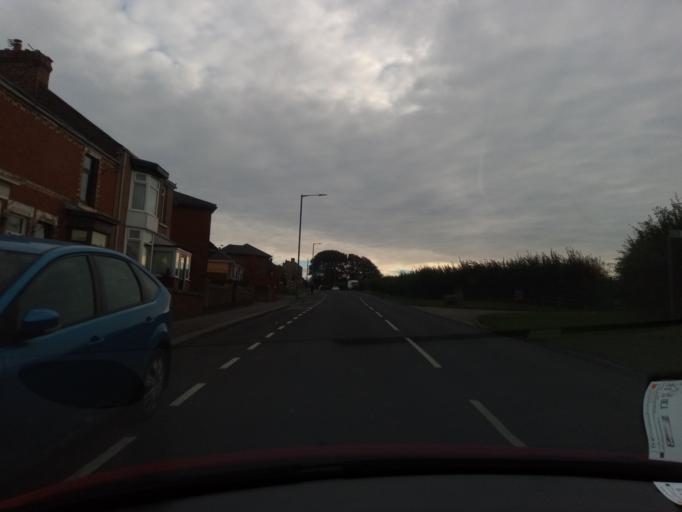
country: GB
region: England
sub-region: County Durham
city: Shildon
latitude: 54.6381
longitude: -1.6574
